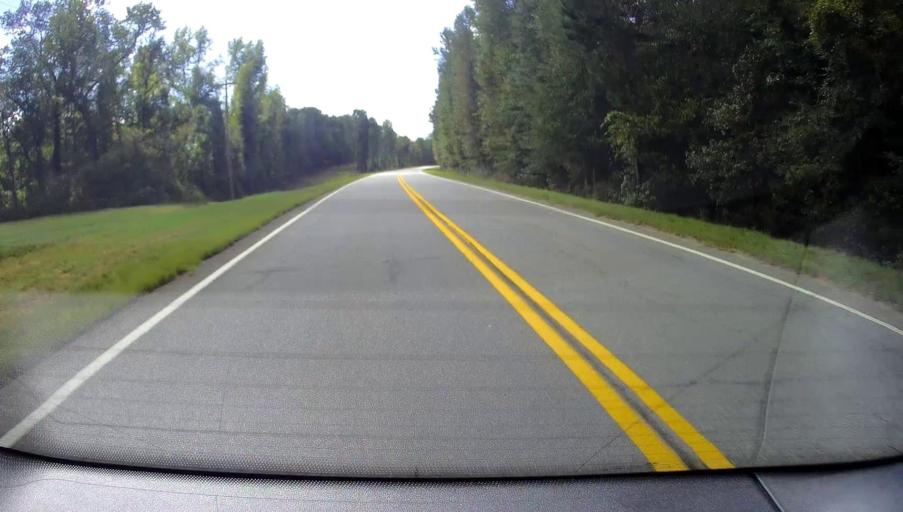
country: US
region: Georgia
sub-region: Jones County
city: Gray
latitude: 32.9655
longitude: -83.4296
